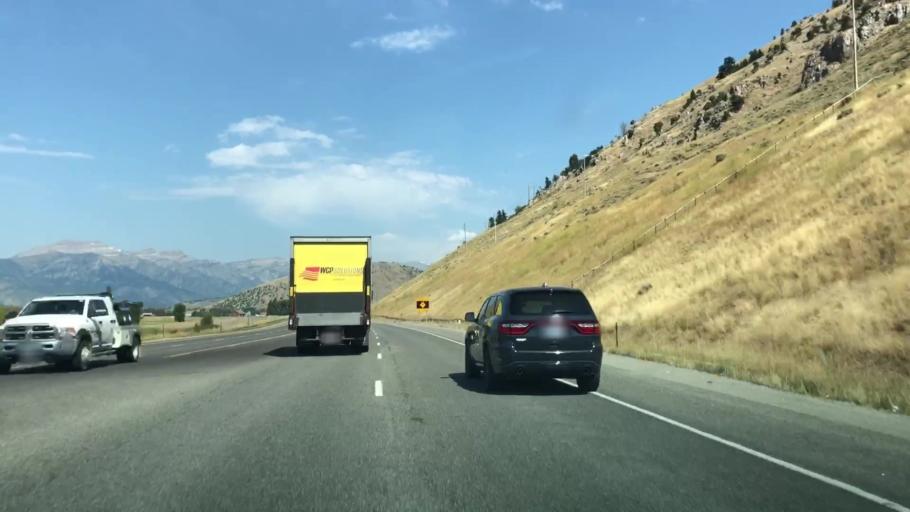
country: US
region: Wyoming
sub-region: Teton County
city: Rafter J Ranch
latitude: 43.4394
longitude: -110.7872
